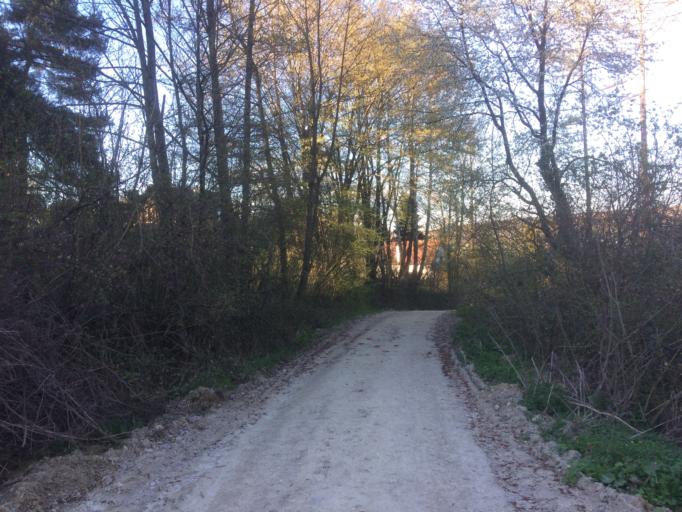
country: AT
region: Lower Austria
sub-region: Politischer Bezirk Wien-Umgebung
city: Gablitz
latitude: 48.2174
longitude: 16.1420
